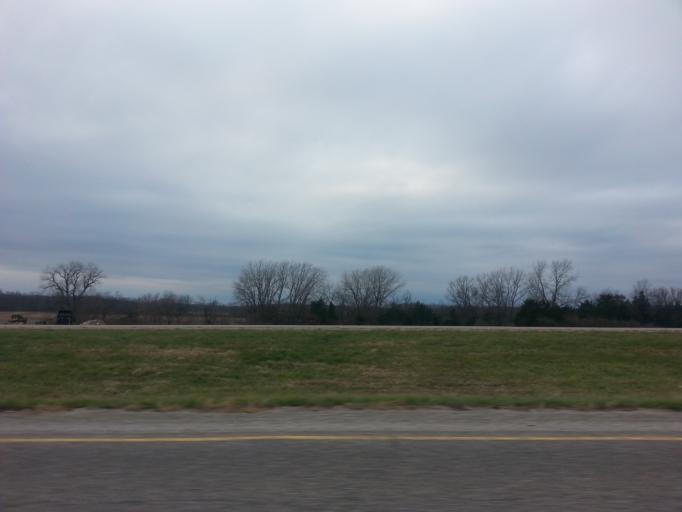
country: US
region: Iowa
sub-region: Henry County
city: Mount Pleasant
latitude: 40.9030
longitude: -91.5516
